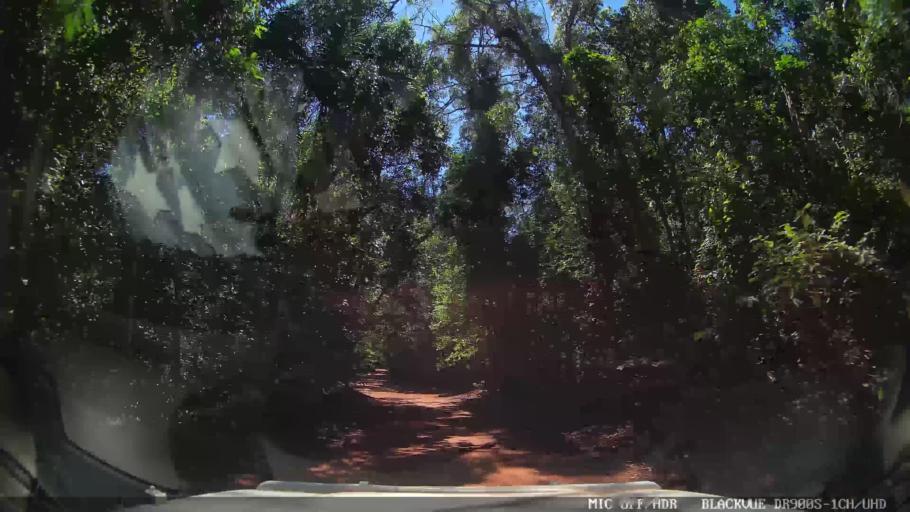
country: AU
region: Queensland
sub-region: Torres
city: Thursday Island
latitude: -10.7781
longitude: 142.4906
